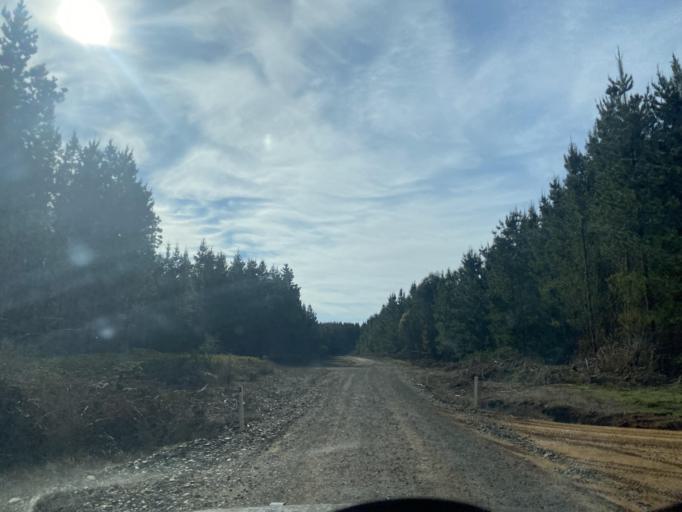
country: AU
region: Victoria
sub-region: Mansfield
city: Mansfield
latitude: -36.8778
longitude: 146.1866
